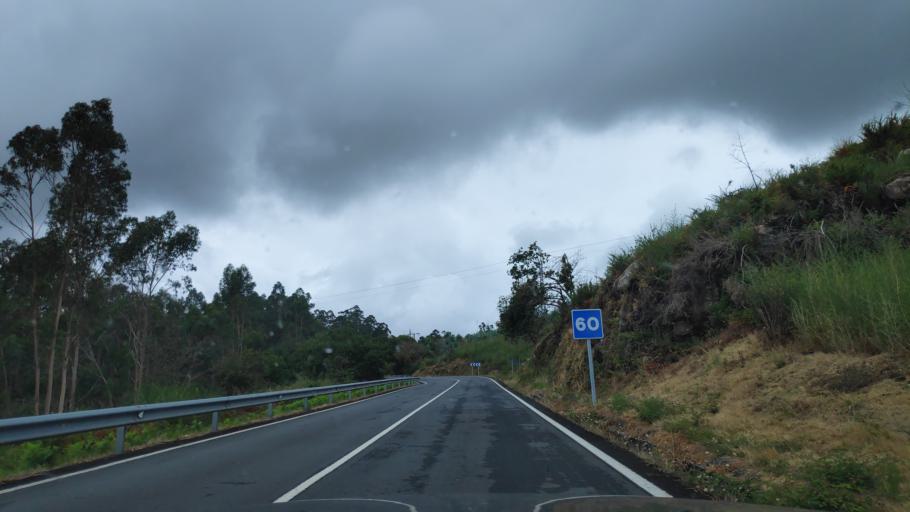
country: ES
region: Galicia
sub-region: Provincia de Pontevedra
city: Catoira
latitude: 42.6958
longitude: -8.7475
